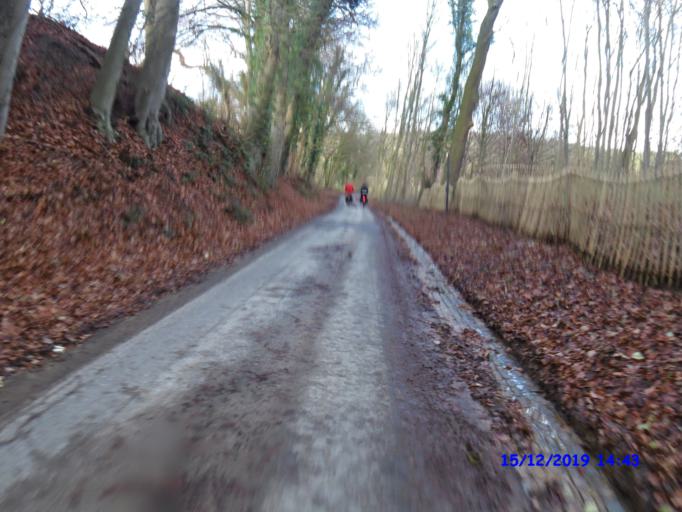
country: BE
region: Flanders
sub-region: Provincie Vlaams-Brabant
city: Beersel
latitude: 50.7499
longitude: 4.3143
